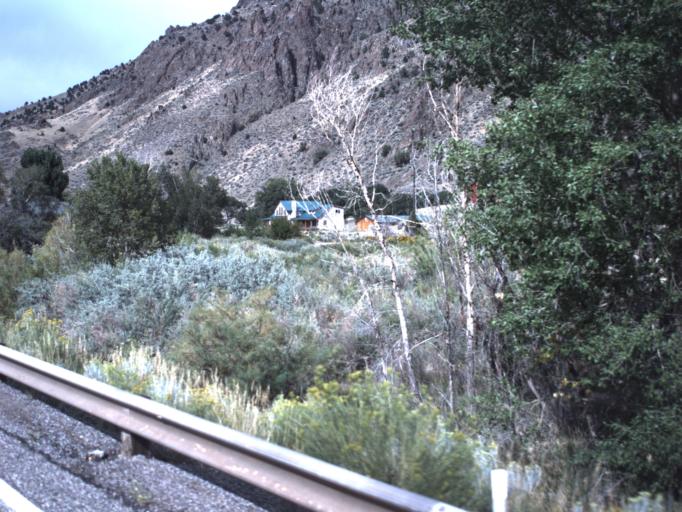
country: US
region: Utah
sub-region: Sevier County
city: Monroe
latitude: 38.5072
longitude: -112.2593
